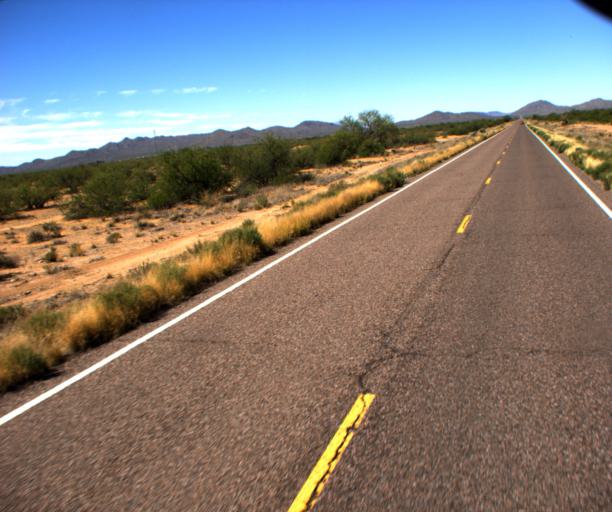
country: US
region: Arizona
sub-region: Yavapai County
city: Congress
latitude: 34.1406
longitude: -112.9074
